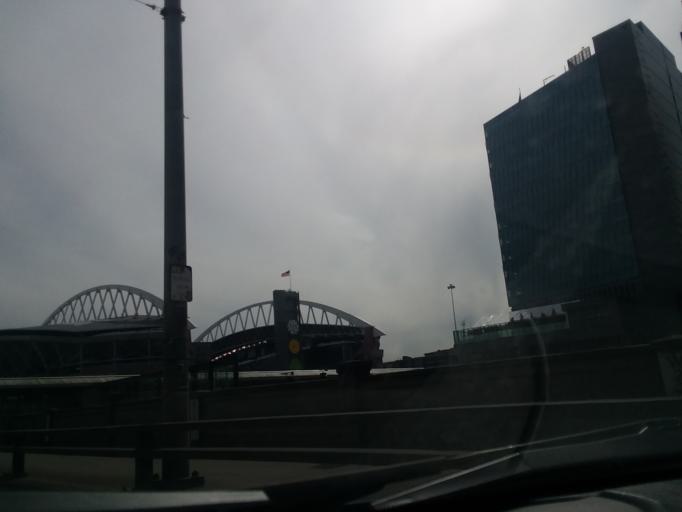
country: US
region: Washington
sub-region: King County
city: Seattle
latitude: 47.5982
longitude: -122.3292
